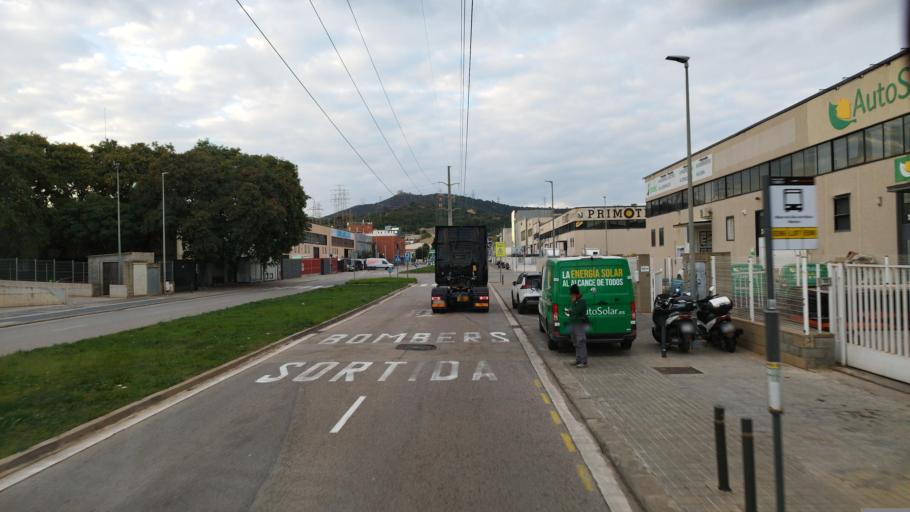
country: ES
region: Catalonia
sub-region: Provincia de Barcelona
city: Sant Boi de Llobregat
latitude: 41.3225
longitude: 2.0354
